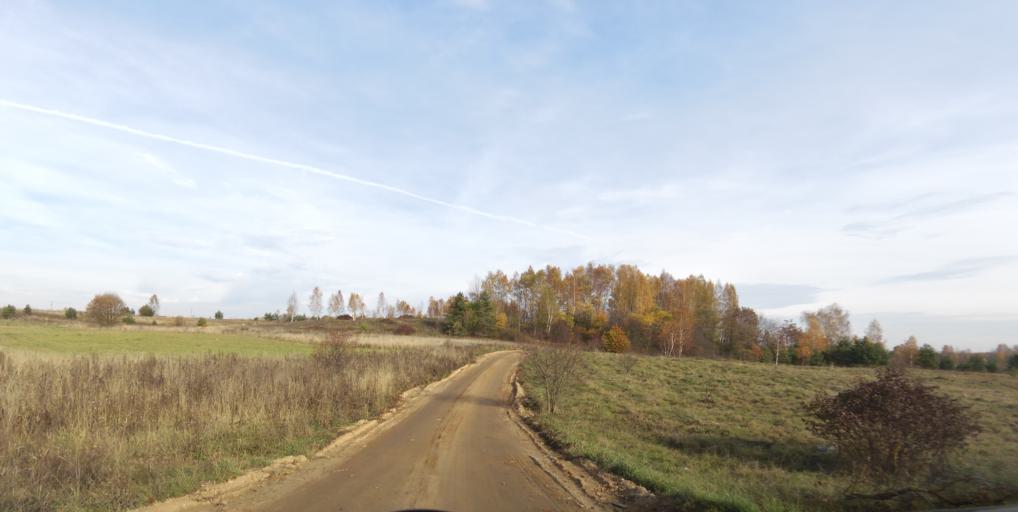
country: LT
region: Vilnius County
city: Pilaite
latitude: 54.7217
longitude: 25.1573
